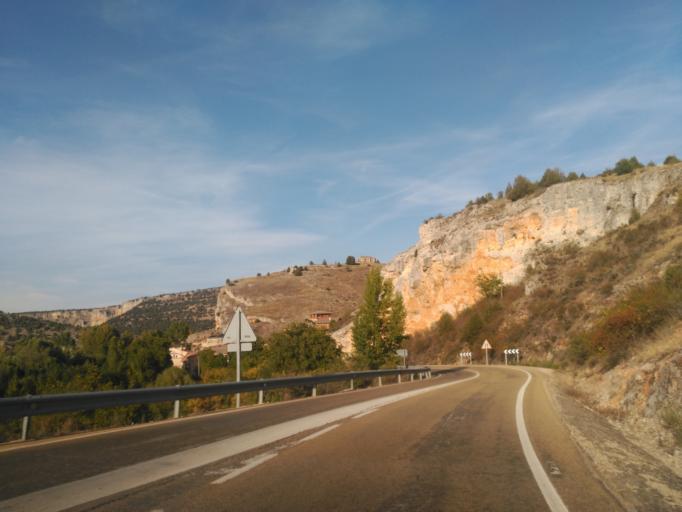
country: ES
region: Castille and Leon
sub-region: Provincia de Soria
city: Ucero
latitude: 41.7150
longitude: -3.0508
